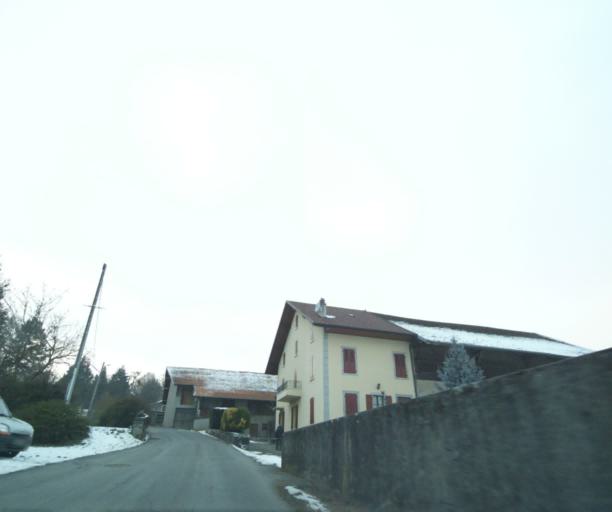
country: FR
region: Rhone-Alpes
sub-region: Departement de la Haute-Savoie
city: Reignier-Esery
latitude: 46.1268
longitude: 6.2568
